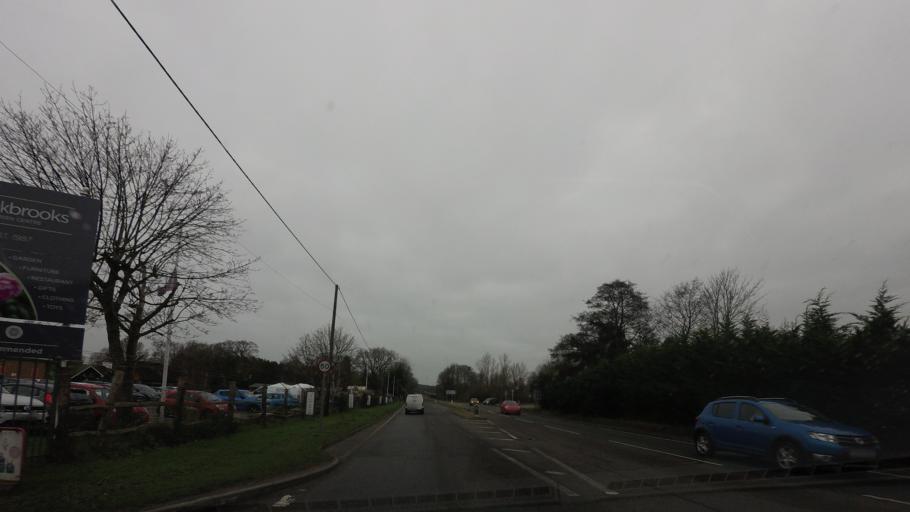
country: GB
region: England
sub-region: East Sussex
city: Battle
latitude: 50.9240
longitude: 0.5336
